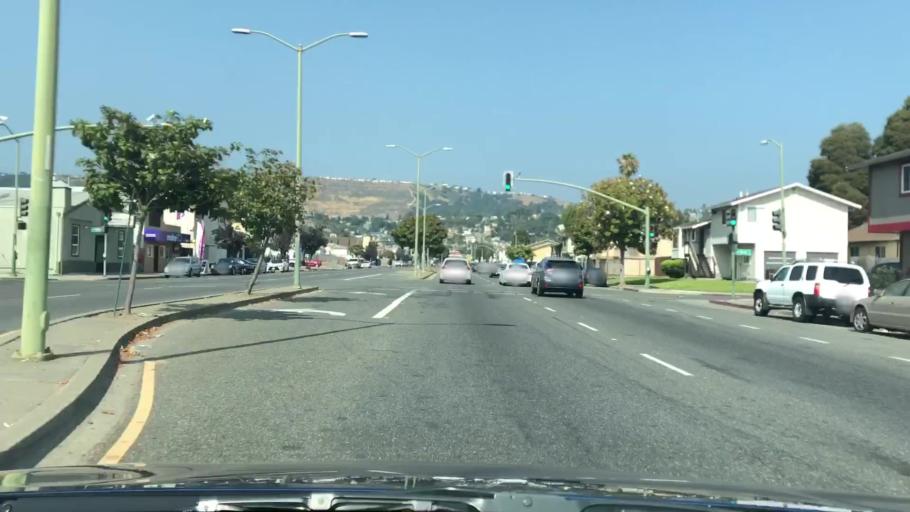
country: US
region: California
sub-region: Alameda County
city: San Leandro
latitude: 37.7624
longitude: -122.1822
